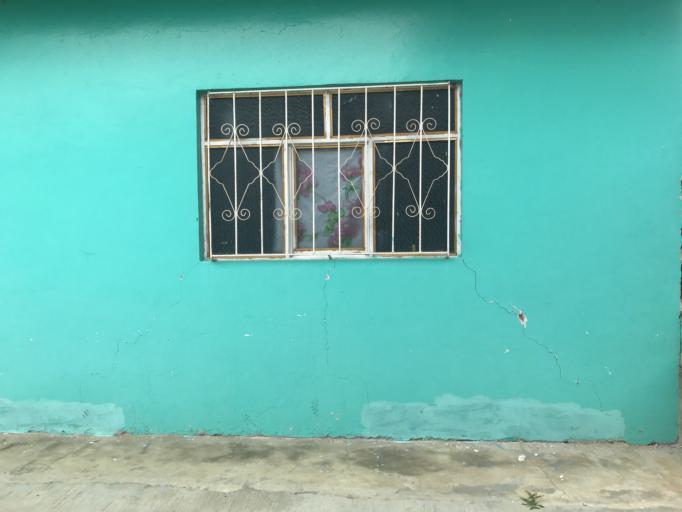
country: MX
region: Puebla
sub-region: Tochimilco
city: San Antonio Alpanocan
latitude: 18.8801
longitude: -98.7169
